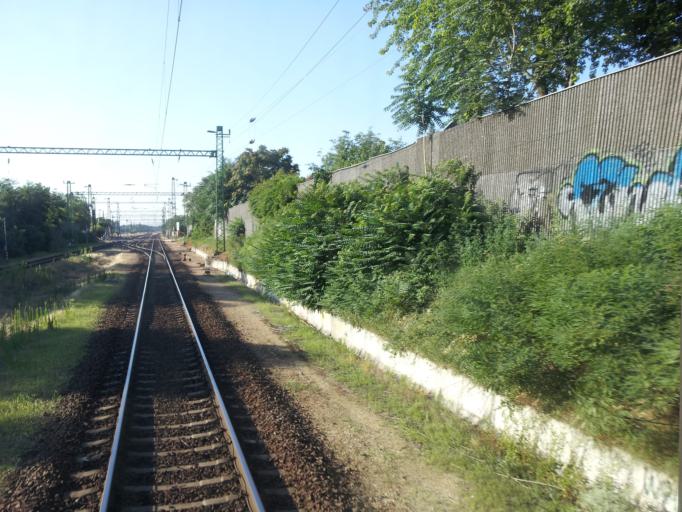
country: HU
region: Budapest
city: Budapest XXIII. keruelet
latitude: 47.4097
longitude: 19.1178
